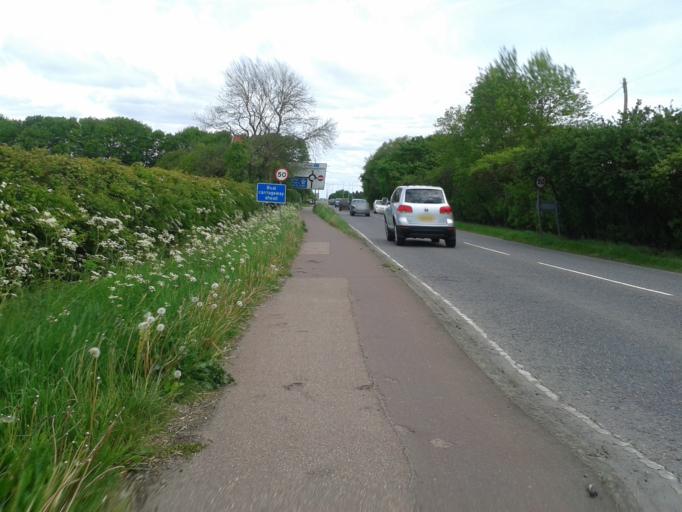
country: GB
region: England
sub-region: Cambridgeshire
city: Barton
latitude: 52.1849
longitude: 0.0694
